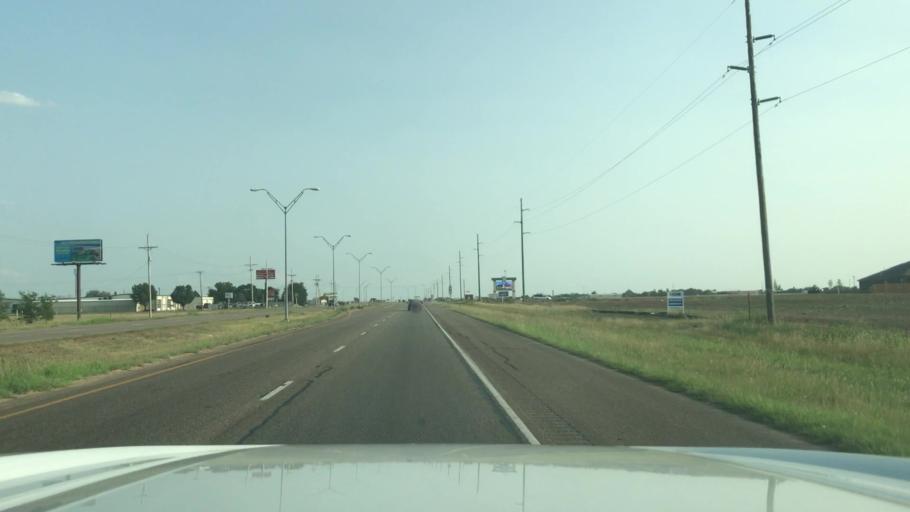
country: US
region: Texas
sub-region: Potter County
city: Bushland
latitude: 35.1281
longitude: -101.9381
